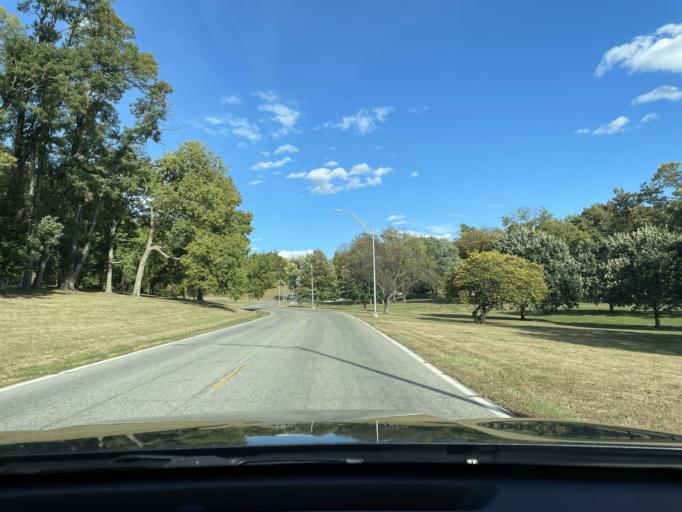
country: US
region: Kansas
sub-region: Doniphan County
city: Elwood
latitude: 39.7183
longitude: -94.8531
